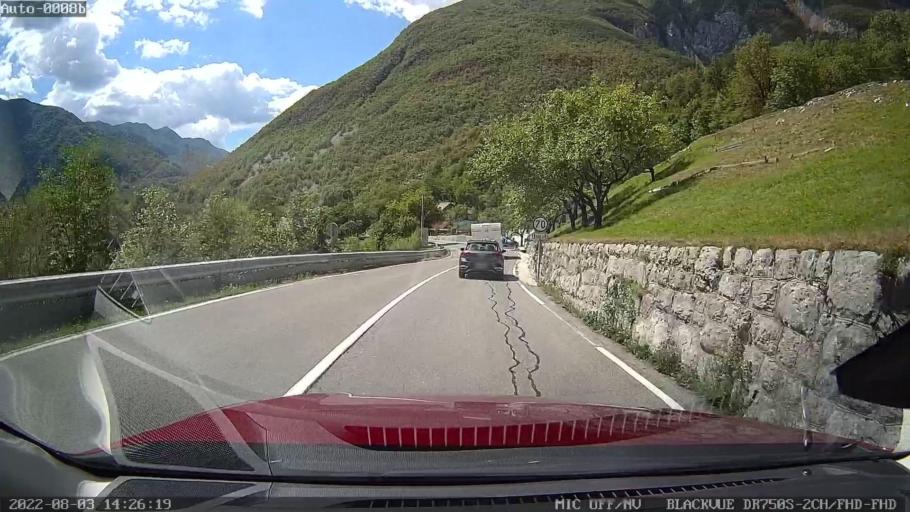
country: SI
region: Bovec
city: Bovec
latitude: 46.3151
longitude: 13.4976
